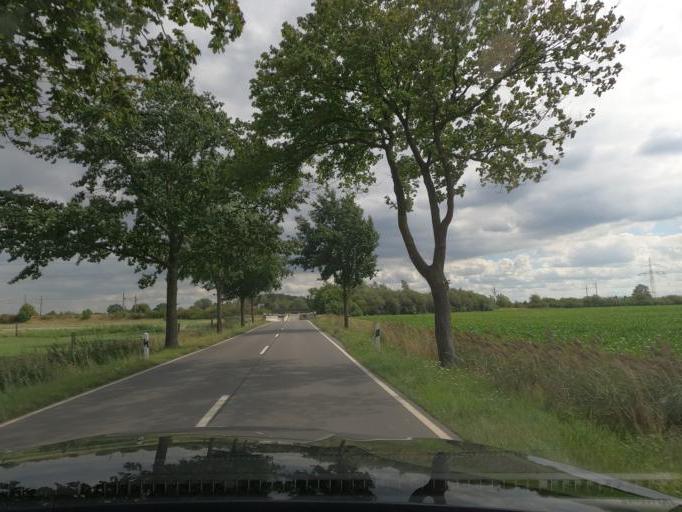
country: DE
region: Lower Saxony
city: Lehrte
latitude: 52.3600
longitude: 10.0110
